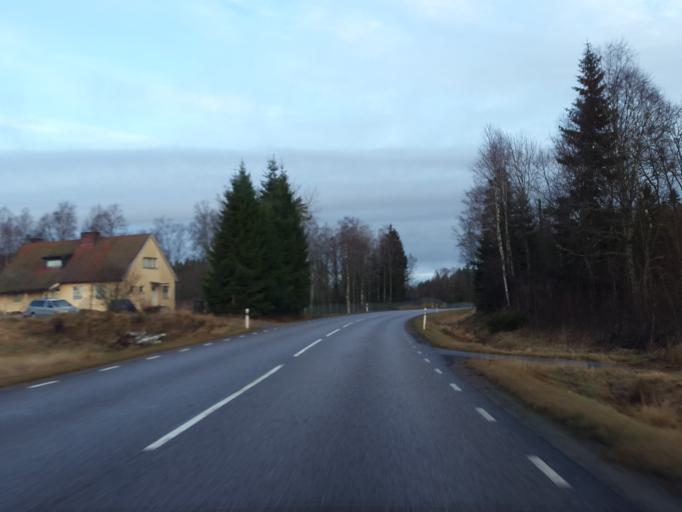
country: SE
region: Vaestra Goetaland
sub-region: Boras Kommun
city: Sandared
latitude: 57.7805
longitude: 12.7820
